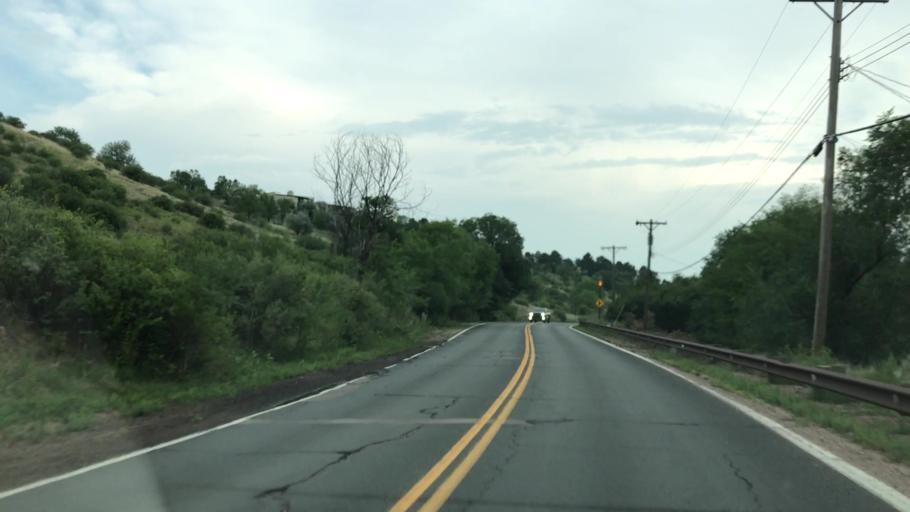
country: US
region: Colorado
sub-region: El Paso County
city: Manitou Springs
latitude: 38.8693
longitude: -104.8678
